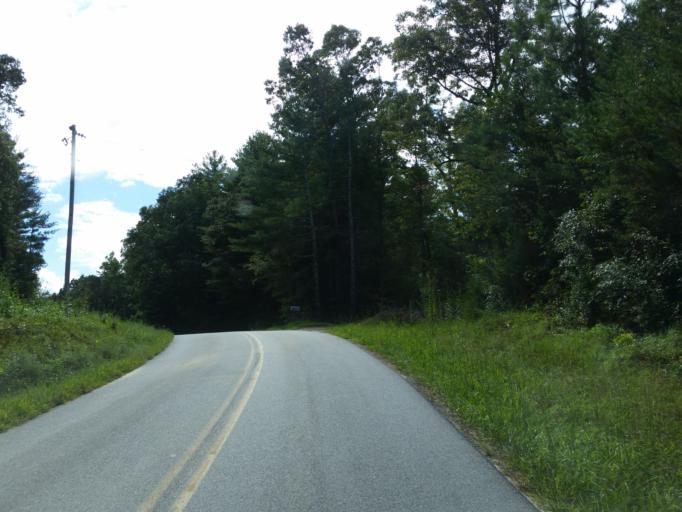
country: US
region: Georgia
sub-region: Fannin County
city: Blue Ridge
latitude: 34.8643
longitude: -84.2394
